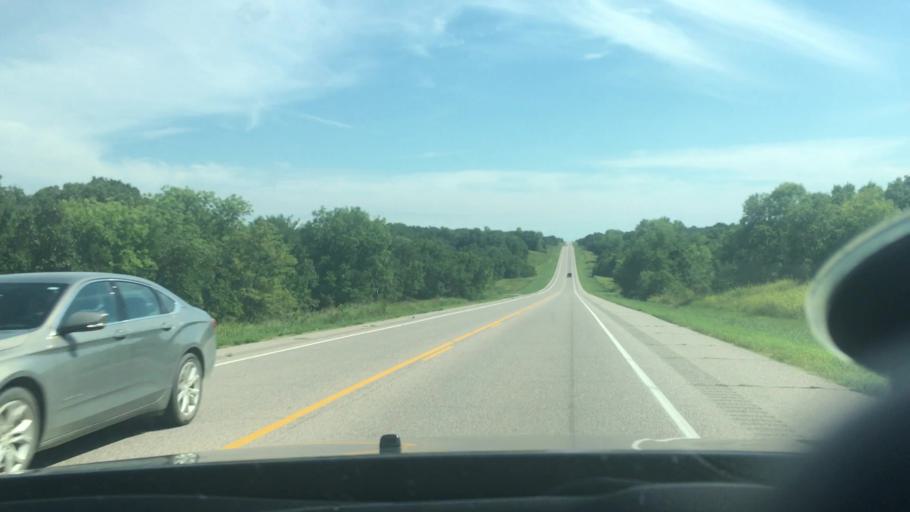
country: US
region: Oklahoma
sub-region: Seminole County
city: Maud
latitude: 35.1139
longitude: -96.6790
